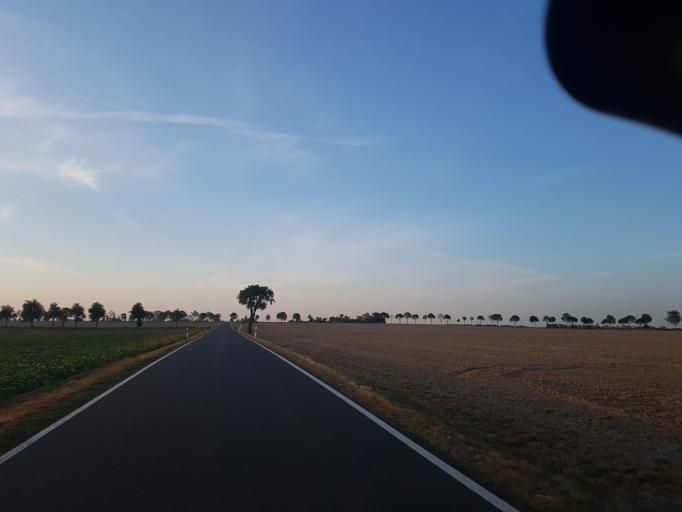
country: DE
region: Saxony
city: Stauchitz
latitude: 51.2826
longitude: 13.1932
